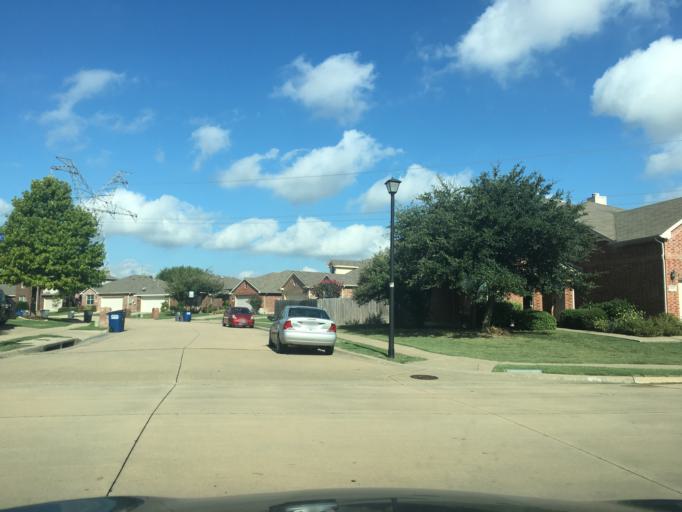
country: US
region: Texas
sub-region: Dallas County
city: Sachse
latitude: 32.9657
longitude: -96.5761
